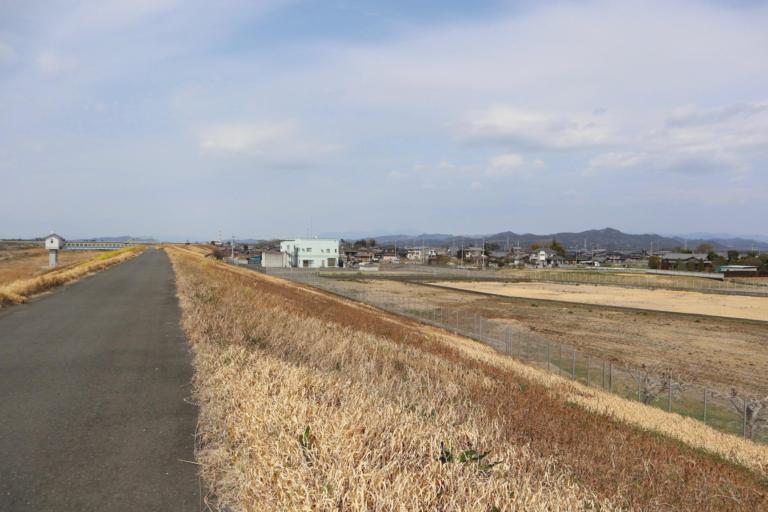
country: JP
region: Gunma
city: Tatebayashi
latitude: 36.2795
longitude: 139.5484
